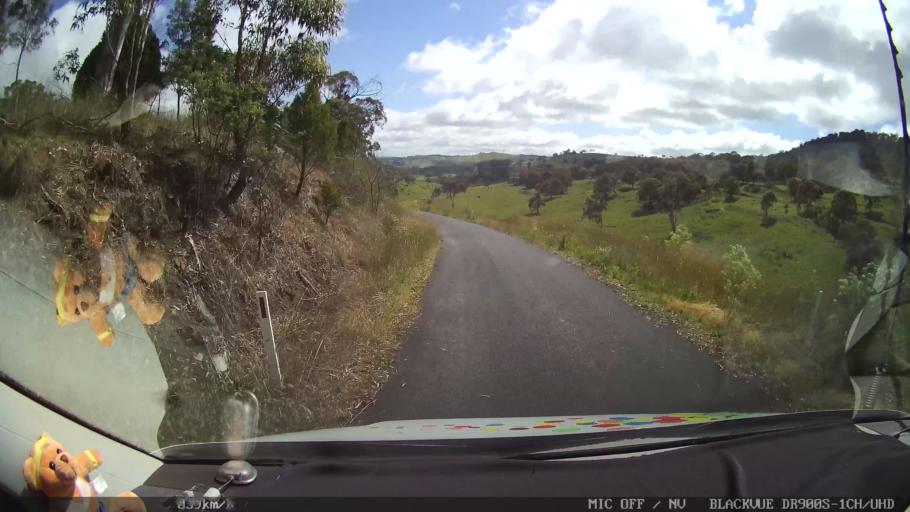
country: AU
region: New South Wales
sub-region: Guyra
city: Guyra
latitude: -30.0019
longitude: 151.6702
